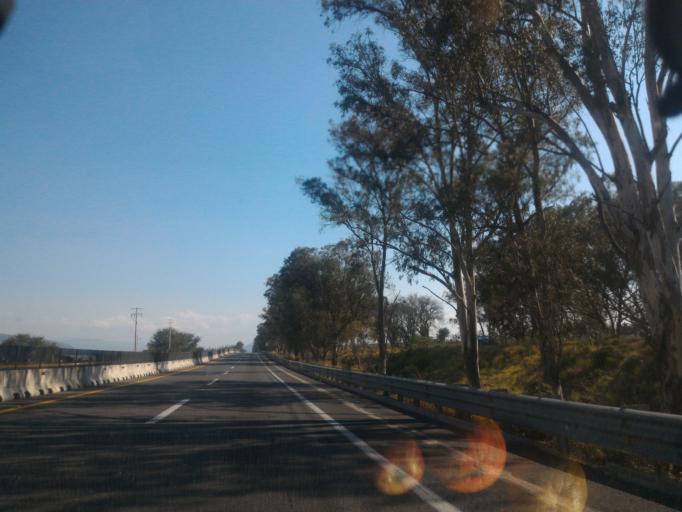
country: MX
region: Jalisco
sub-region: Zapotlan el Grande
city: Ciudad Guzman [CERESO]
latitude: 19.6297
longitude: -103.4655
